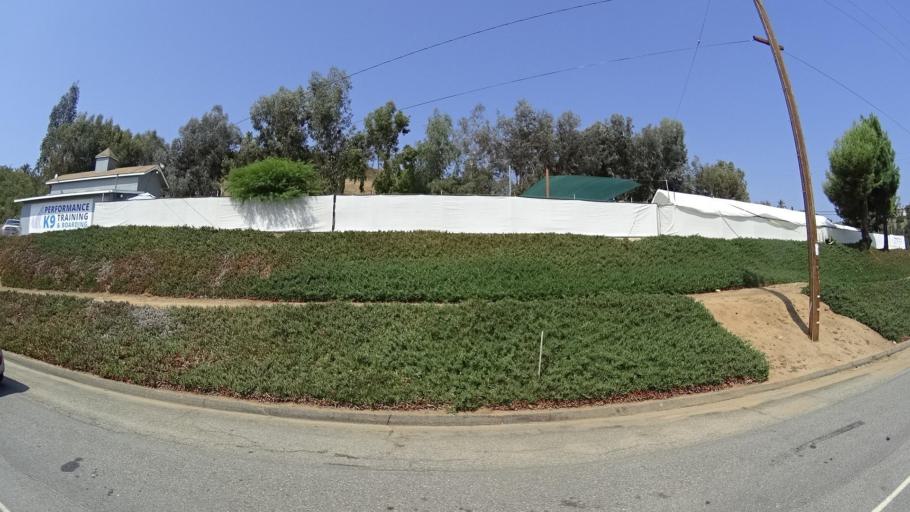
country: US
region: California
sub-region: San Diego County
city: Bonsall
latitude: 33.2750
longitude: -117.2359
